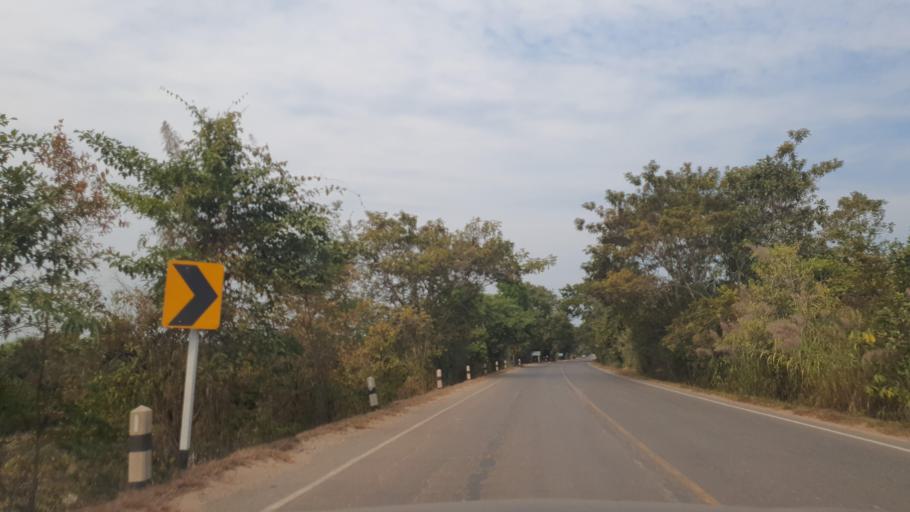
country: TH
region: Changwat Bueng Kan
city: Bung Khla
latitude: 18.1855
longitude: 104.0568
